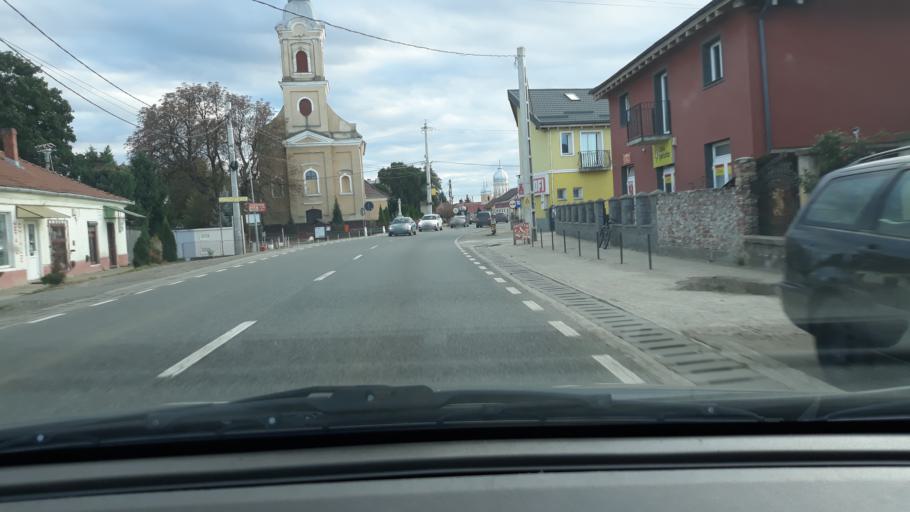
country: RO
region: Bihor
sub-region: Comuna Biharea
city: Biharea
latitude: 47.1537
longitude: 21.9206
